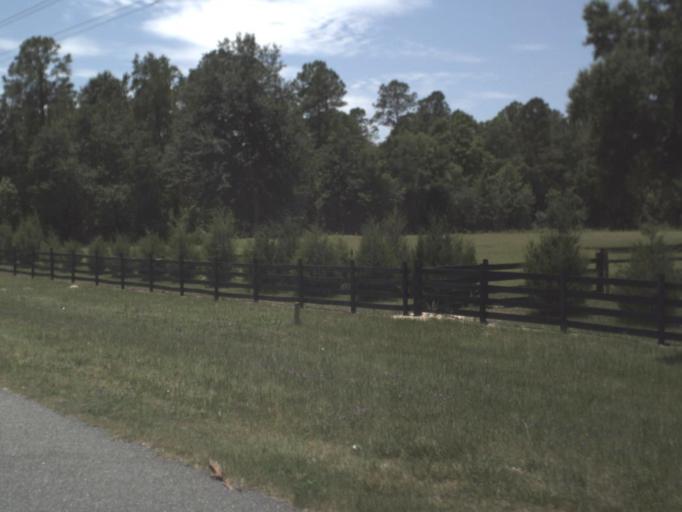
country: US
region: Florida
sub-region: Dixie County
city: Cross City
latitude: 29.7437
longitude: -82.9847
